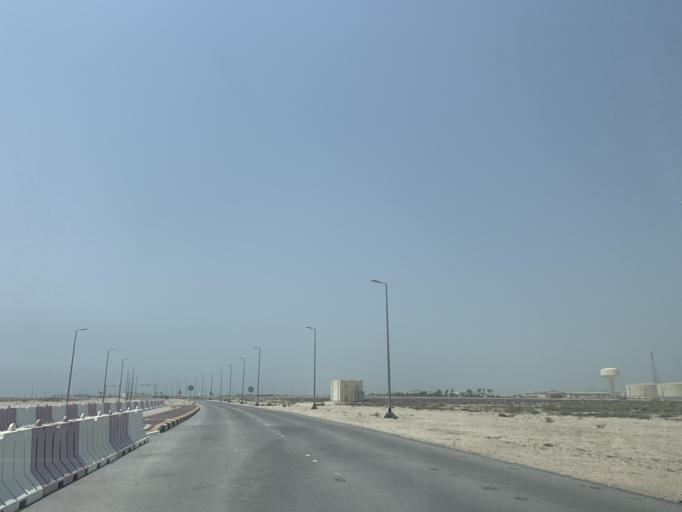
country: BH
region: Central Governorate
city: Dar Kulayb
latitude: 25.8422
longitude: 50.5928
